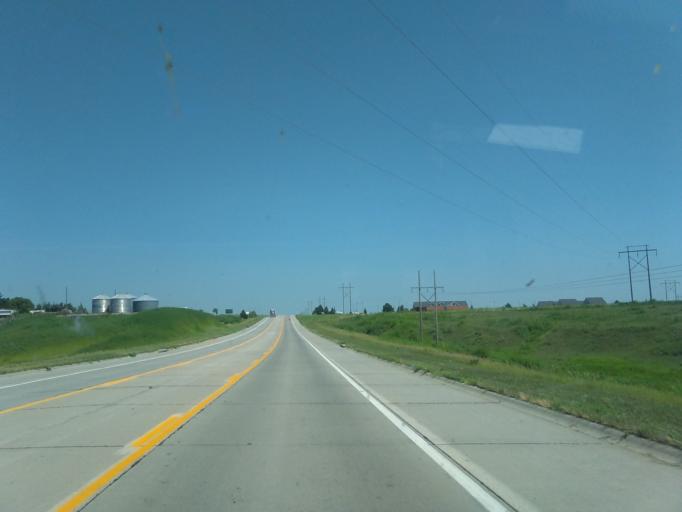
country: US
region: Nebraska
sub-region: Red Willow County
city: McCook
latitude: 40.2238
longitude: -100.6500
